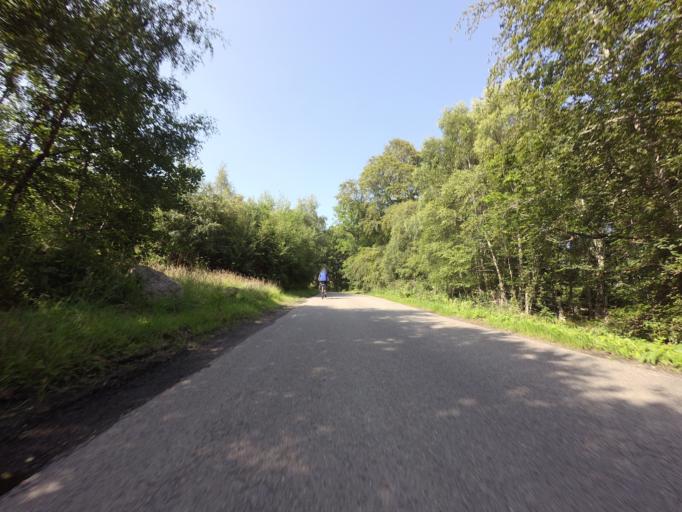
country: GB
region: Scotland
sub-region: Highland
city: Evanton
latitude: 57.6482
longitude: -4.3516
